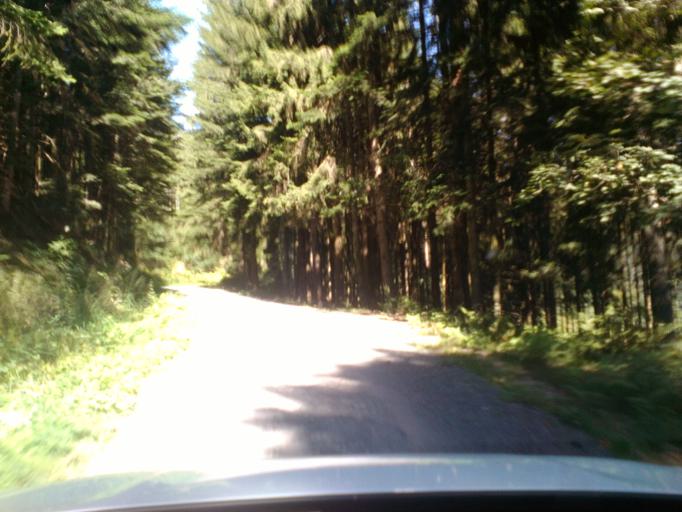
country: FR
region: Lorraine
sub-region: Departement des Vosges
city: Senones
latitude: 48.4070
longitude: 6.9762
